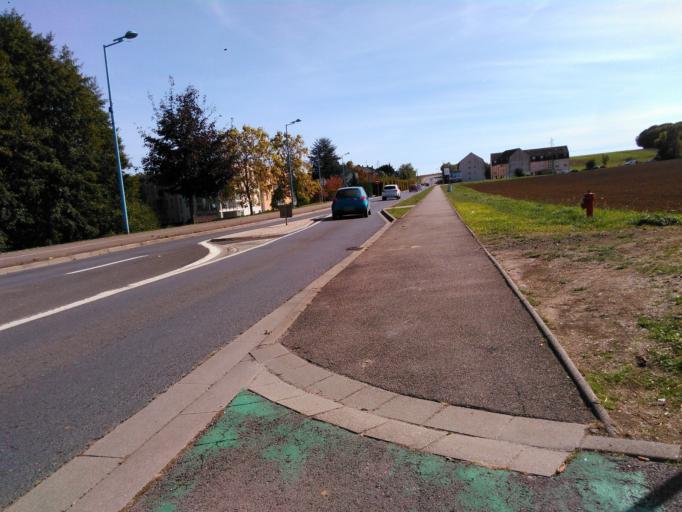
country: FR
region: Lorraine
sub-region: Departement de la Moselle
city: Hettange-Grande
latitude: 49.3961
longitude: 6.1640
